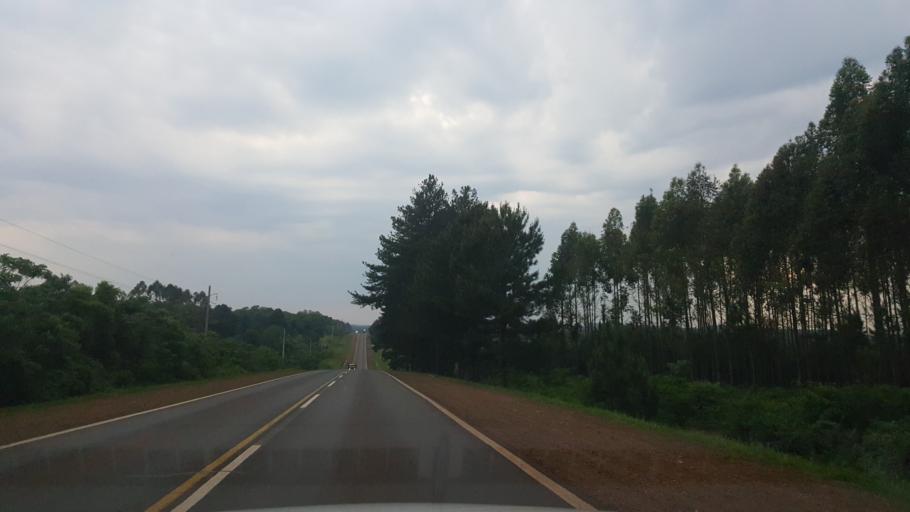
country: AR
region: Misiones
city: Jardin America
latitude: -27.0188
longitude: -55.1975
